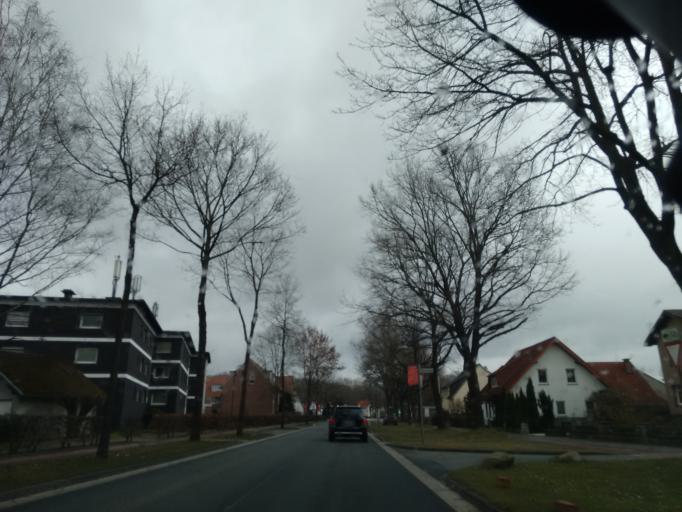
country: DE
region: North Rhine-Westphalia
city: Bad Lippspringe
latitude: 51.7632
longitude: 8.7858
